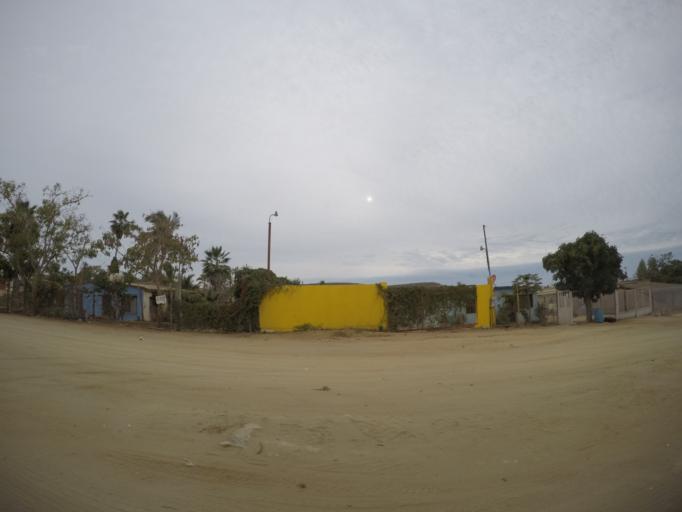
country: MX
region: Baja California Sur
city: Todos Santos
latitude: 23.4429
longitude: -110.2240
